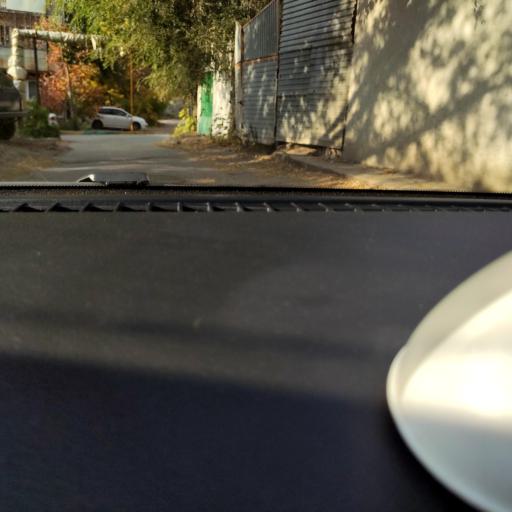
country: RU
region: Samara
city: Samara
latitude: 53.2002
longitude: 50.1585
